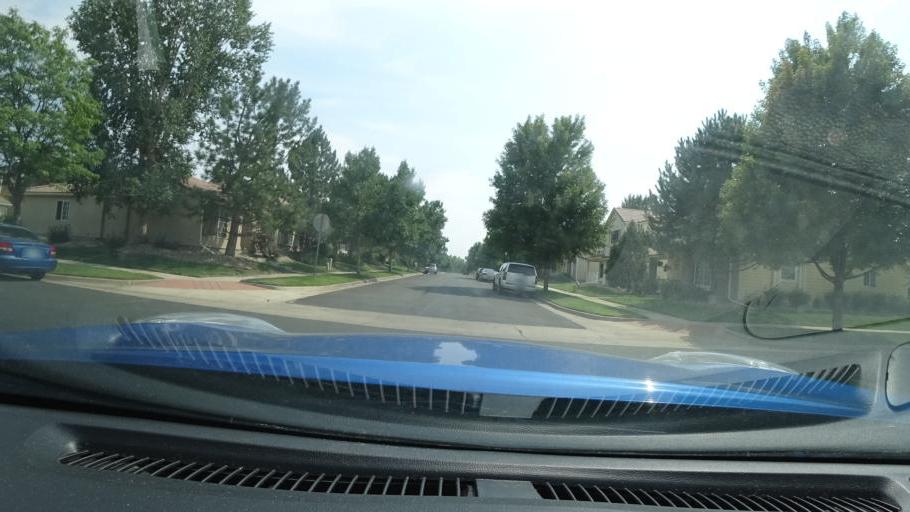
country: US
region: Colorado
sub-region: Adams County
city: Aurora
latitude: 39.7811
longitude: -104.7370
